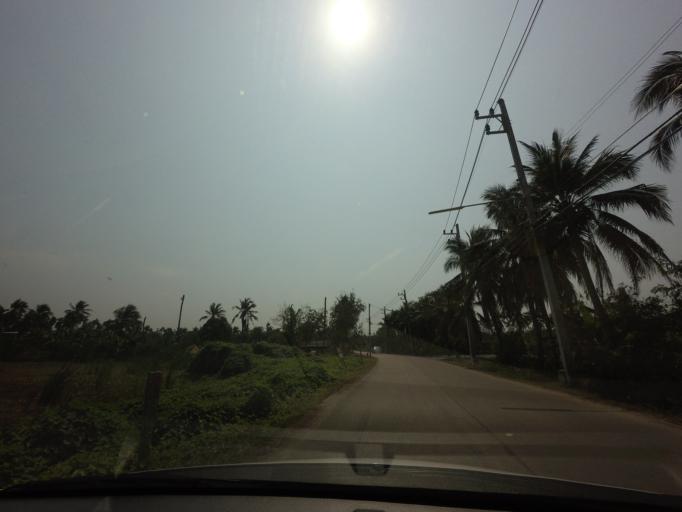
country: TH
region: Nakhon Pathom
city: Sam Phran
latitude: 13.7578
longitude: 100.2600
